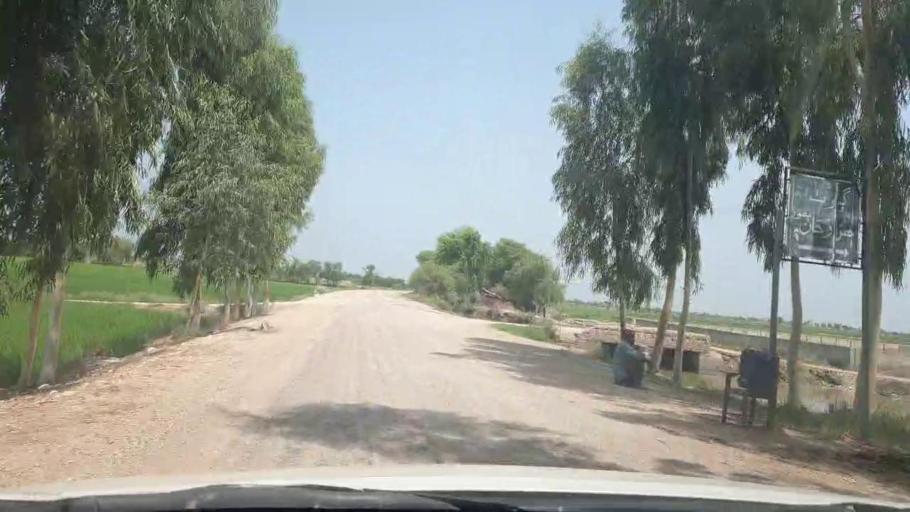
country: PK
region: Sindh
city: Rustam jo Goth
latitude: 28.0300
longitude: 68.7891
